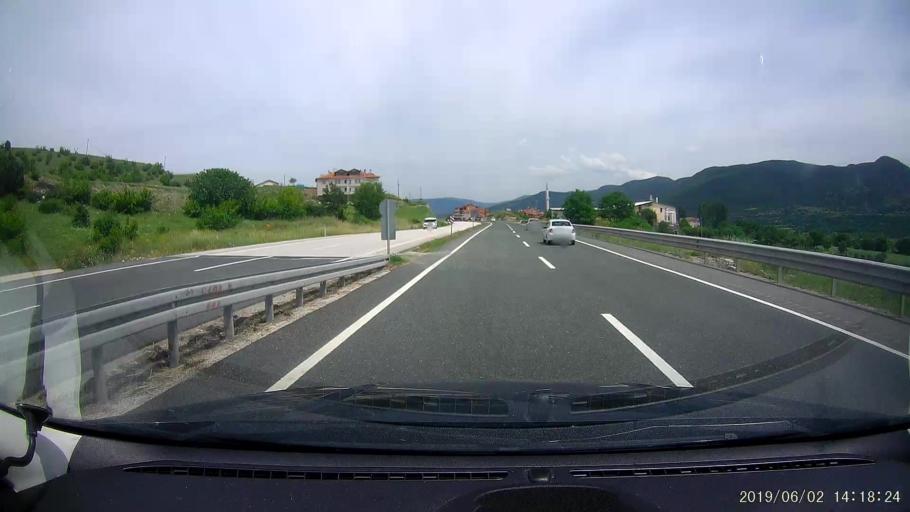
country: TR
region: Kastamonu
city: Tosya
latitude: 40.9572
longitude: 33.9546
